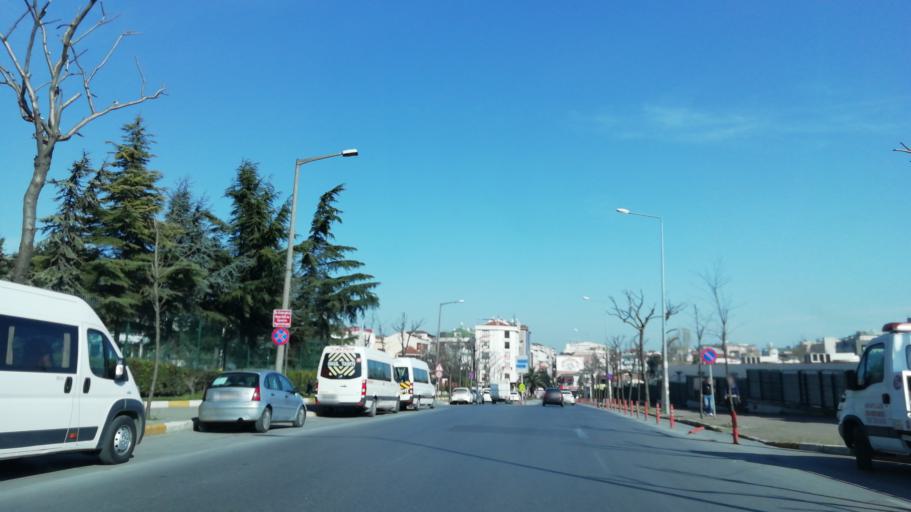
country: TR
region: Istanbul
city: Bahcelievler
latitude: 40.9946
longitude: 28.8330
